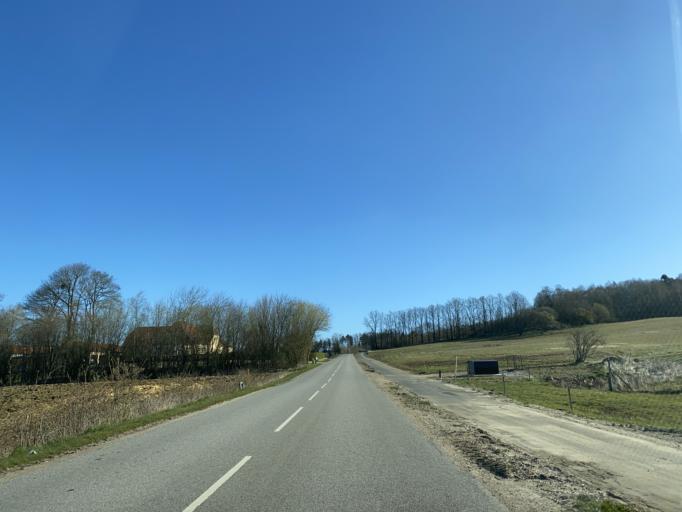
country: DK
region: Central Jutland
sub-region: Favrskov Kommune
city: Ulstrup
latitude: 56.3794
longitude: 9.7402
